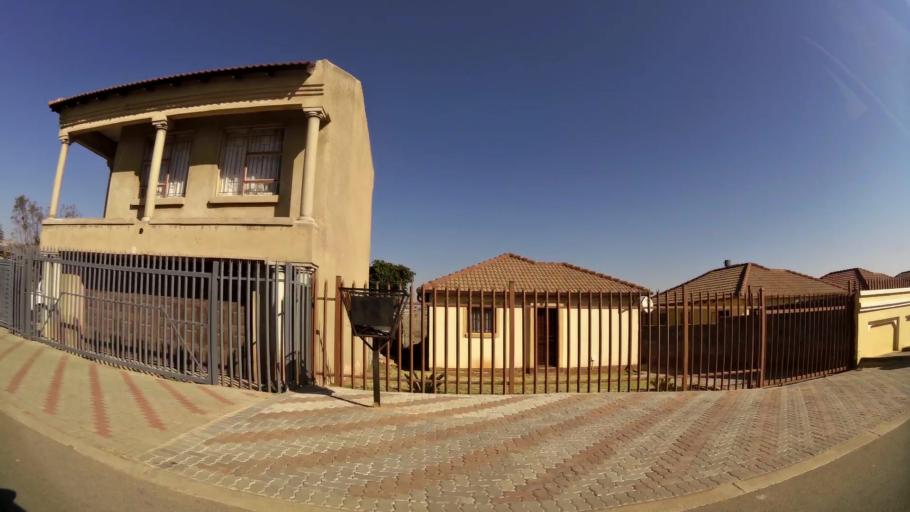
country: ZA
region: Gauteng
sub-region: Ekurhuleni Metropolitan Municipality
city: Tembisa
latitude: -26.0394
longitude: 28.1958
